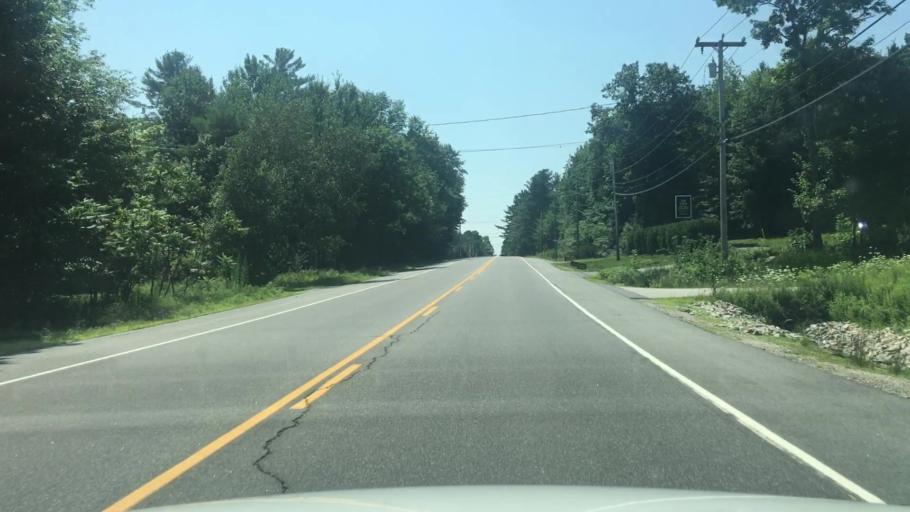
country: US
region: Maine
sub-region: Cumberland County
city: Cumberland Center
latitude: 43.8636
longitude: -70.3235
